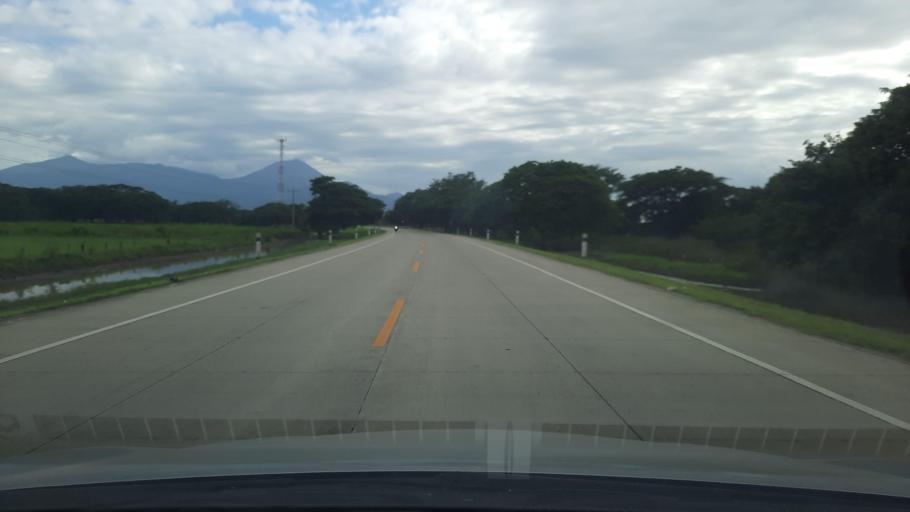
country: NI
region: Chinandega
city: Somotillo
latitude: 12.8360
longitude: -86.8914
